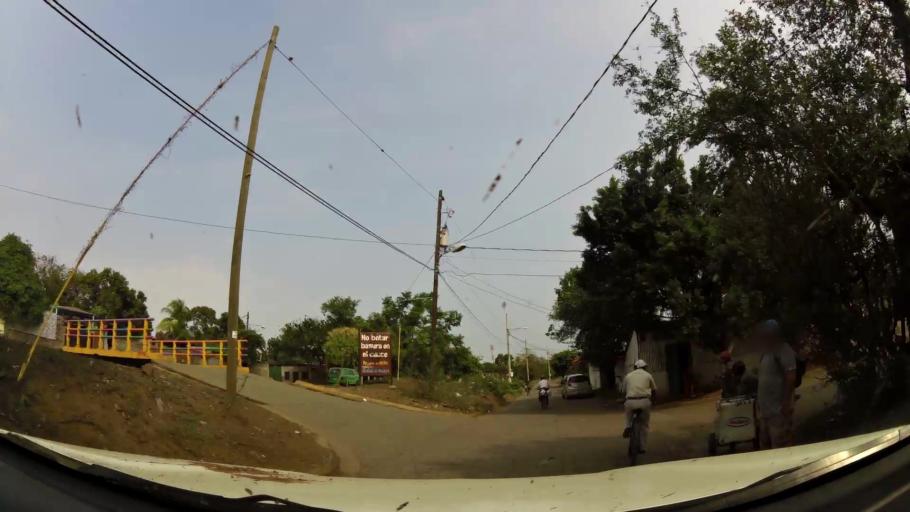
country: NI
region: Masaya
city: Masaya
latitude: 11.9709
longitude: -86.0867
